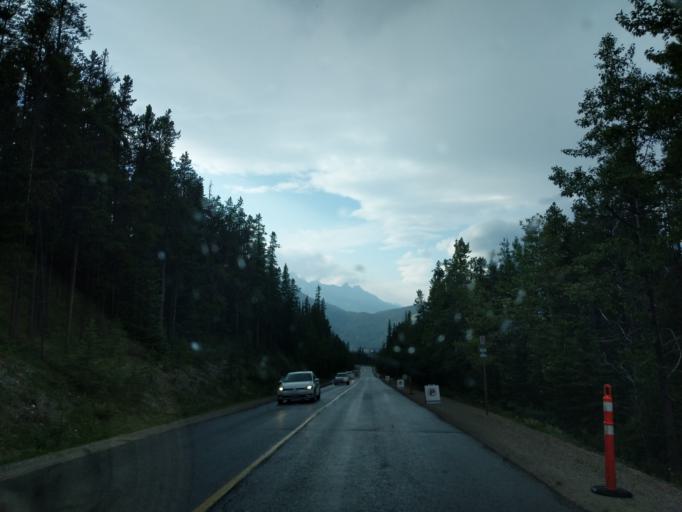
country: CA
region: Alberta
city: Banff
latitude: 51.1560
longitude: -115.5636
